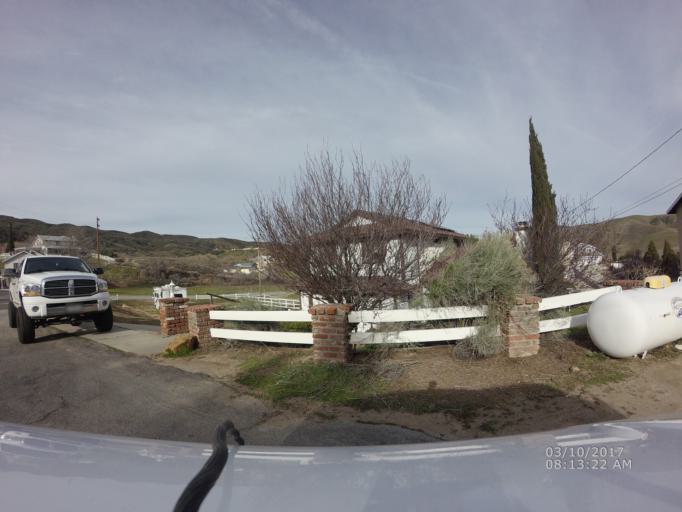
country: US
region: California
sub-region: Los Angeles County
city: Green Valley
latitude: 34.6605
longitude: -118.3965
